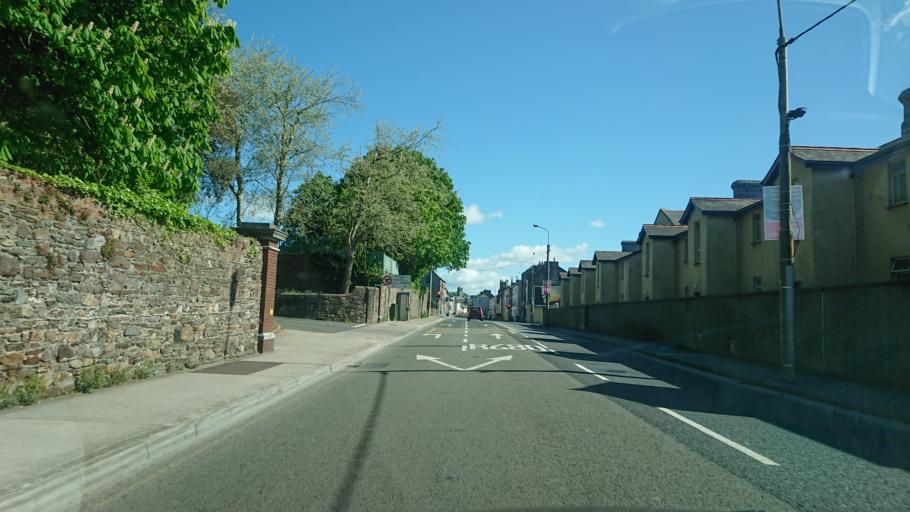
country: IE
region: Munster
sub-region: Waterford
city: Waterford
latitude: 52.2536
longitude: -7.1151
